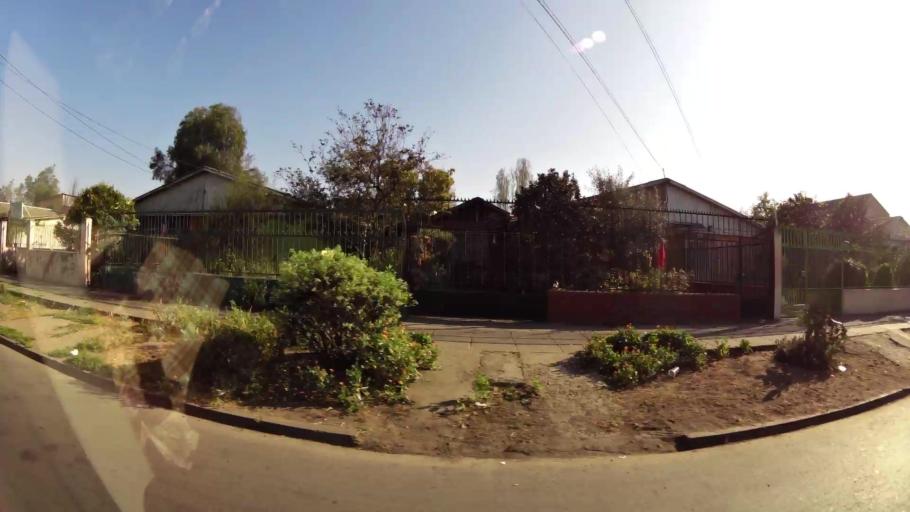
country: CL
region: Santiago Metropolitan
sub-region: Provincia de Santiago
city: Santiago
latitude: -33.3840
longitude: -70.6619
